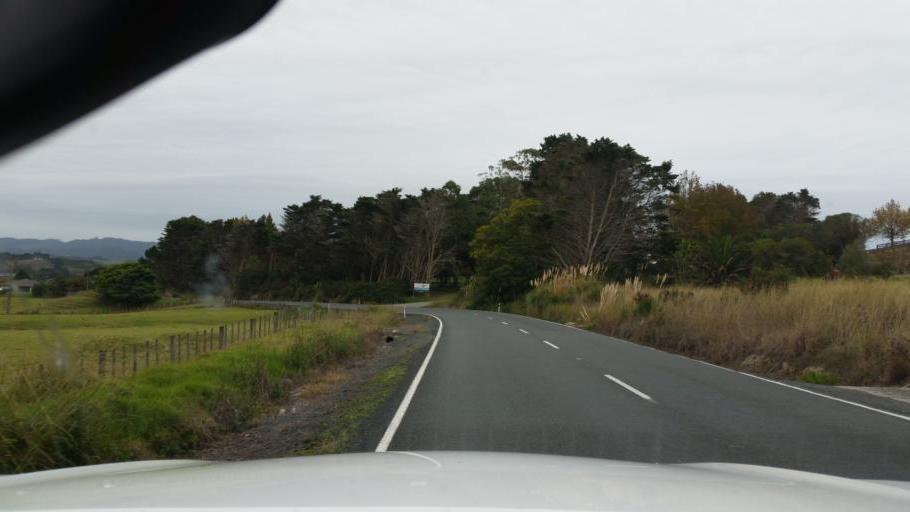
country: NZ
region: Auckland
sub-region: Auckland
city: Wellsford
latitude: -36.1405
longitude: 174.5861
